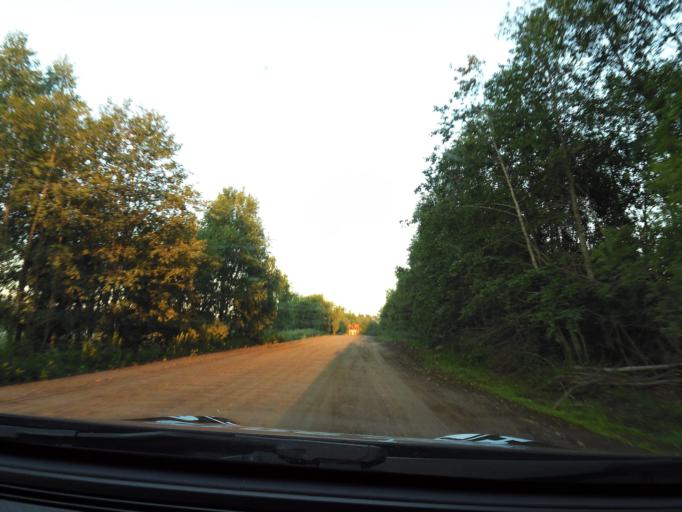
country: RU
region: Leningrad
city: Voznesen'ye
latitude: 60.9063
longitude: 35.4994
